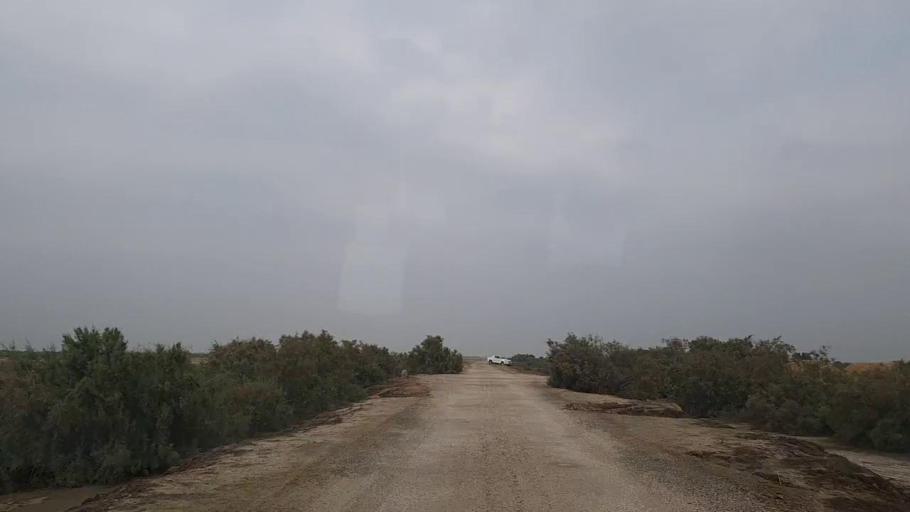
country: PK
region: Sindh
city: Mirpur Sakro
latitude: 24.6237
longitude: 67.7182
